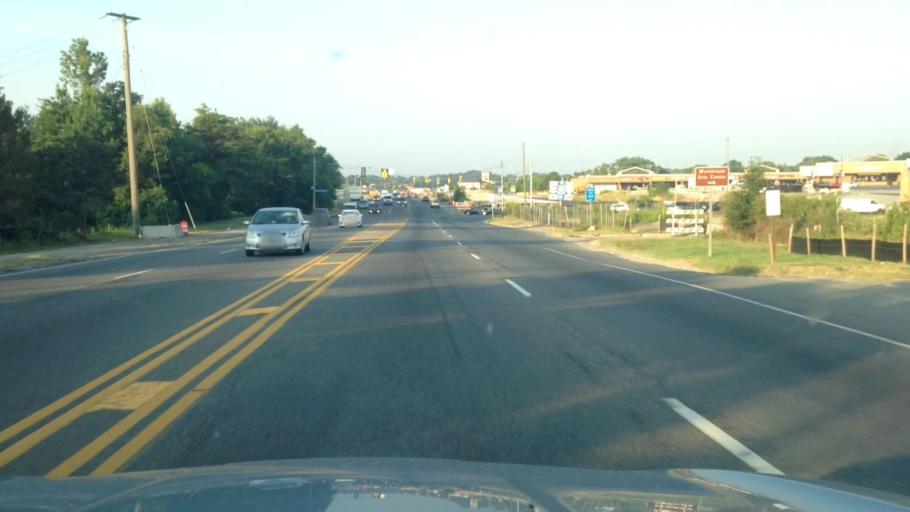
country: US
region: Virginia
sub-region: Prince William County
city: Woodbridge
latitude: 38.6630
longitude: -77.2461
